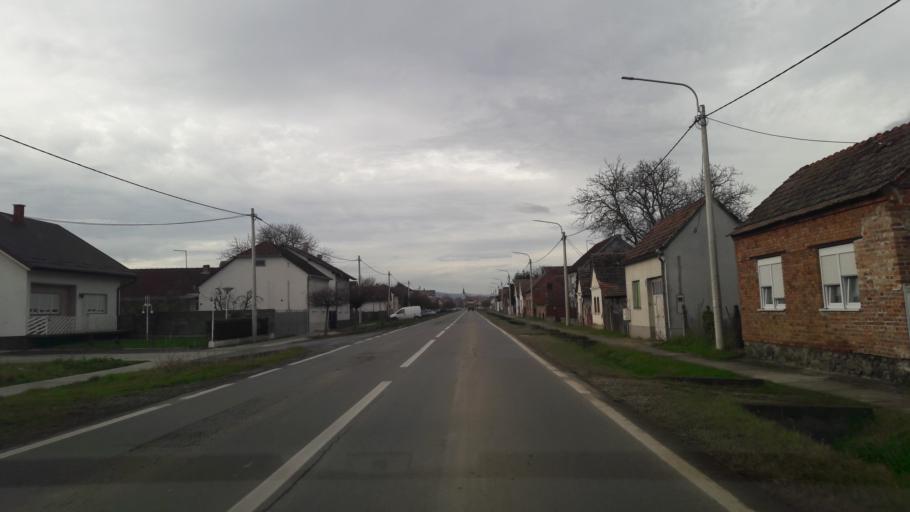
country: HR
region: Osjecko-Baranjska
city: Fericanci
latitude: 45.5237
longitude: 17.9911
